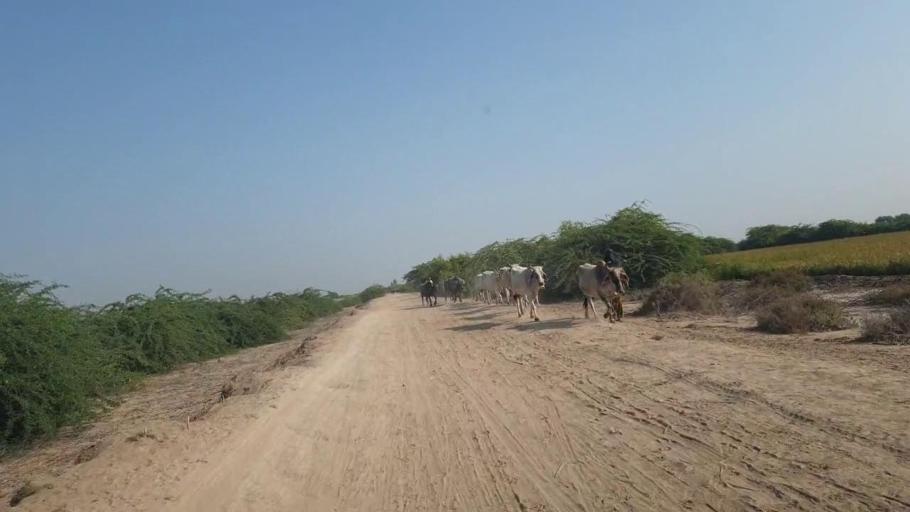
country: PK
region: Sindh
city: Badin
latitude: 24.4630
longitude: 68.7377
